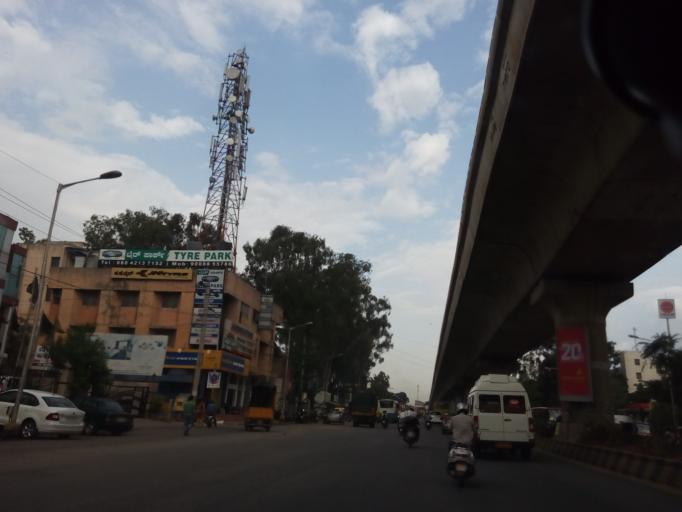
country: IN
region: Karnataka
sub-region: Bangalore Urban
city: Bangalore
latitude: 13.0270
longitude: 77.5435
